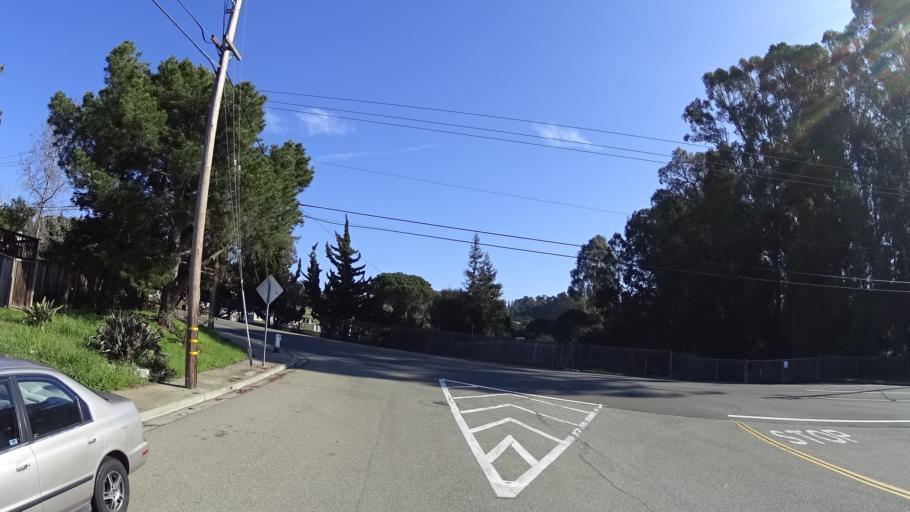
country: US
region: California
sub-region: Alameda County
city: Fairview
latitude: 37.6745
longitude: -122.0519
